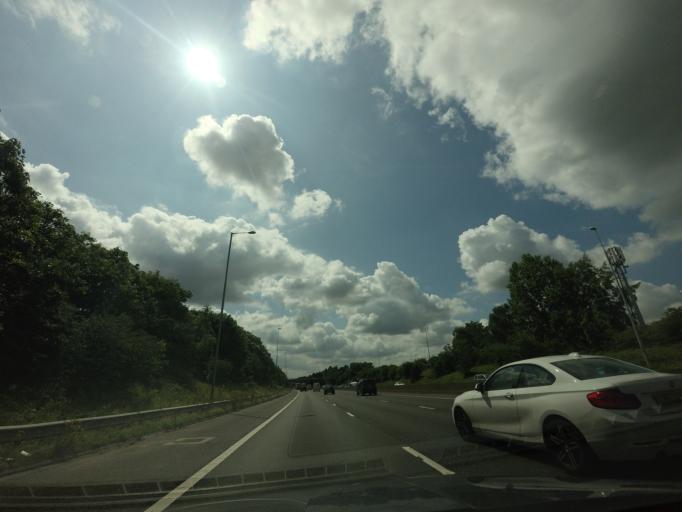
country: GB
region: England
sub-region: Borough of Wigan
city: Shevington
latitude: 53.5732
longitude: -2.6975
